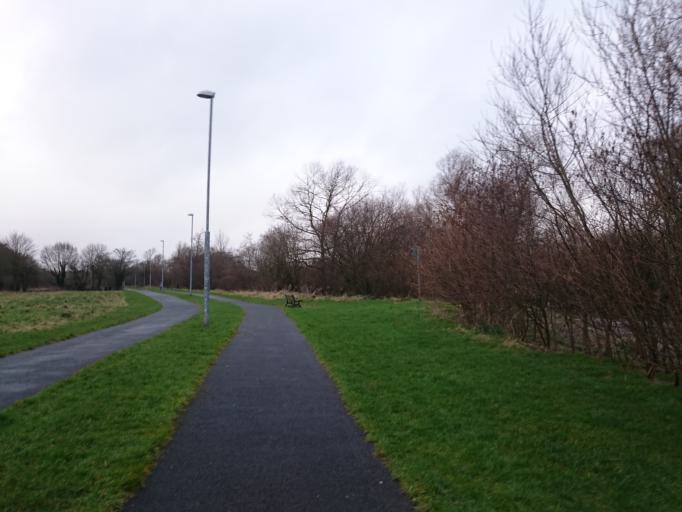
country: IE
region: Leinster
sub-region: Kilkenny
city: Kilkenny
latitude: 52.6652
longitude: -7.2555
